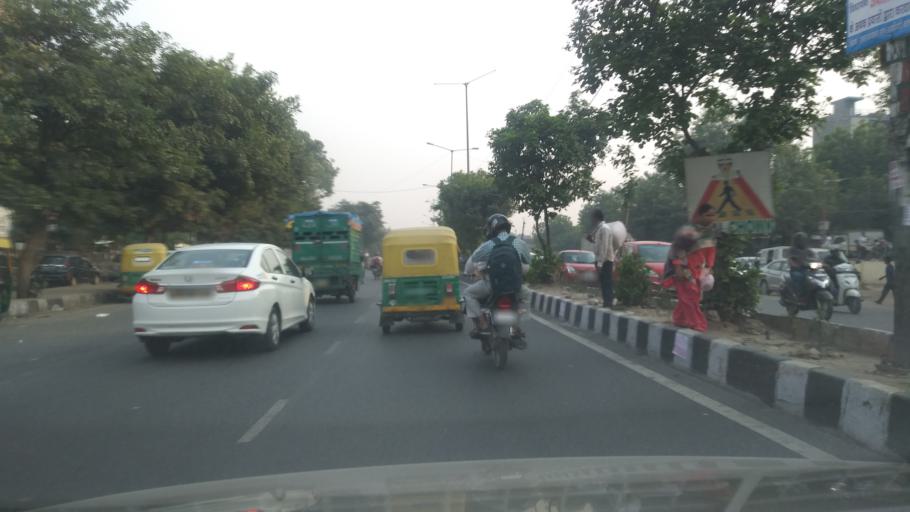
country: IN
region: Uttar Pradesh
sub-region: Gautam Buddha Nagar
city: Noida
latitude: 28.5347
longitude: 77.2684
